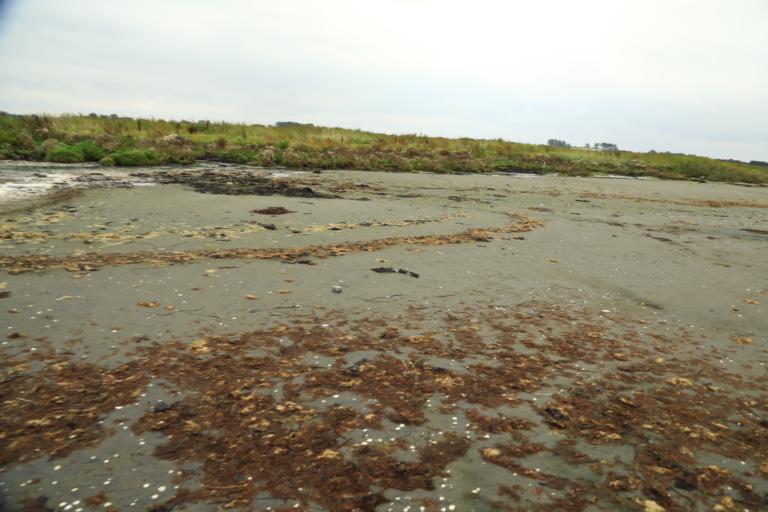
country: SE
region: Halland
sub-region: Varbergs Kommun
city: Tvaaker
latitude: 56.9916
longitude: 12.3553
